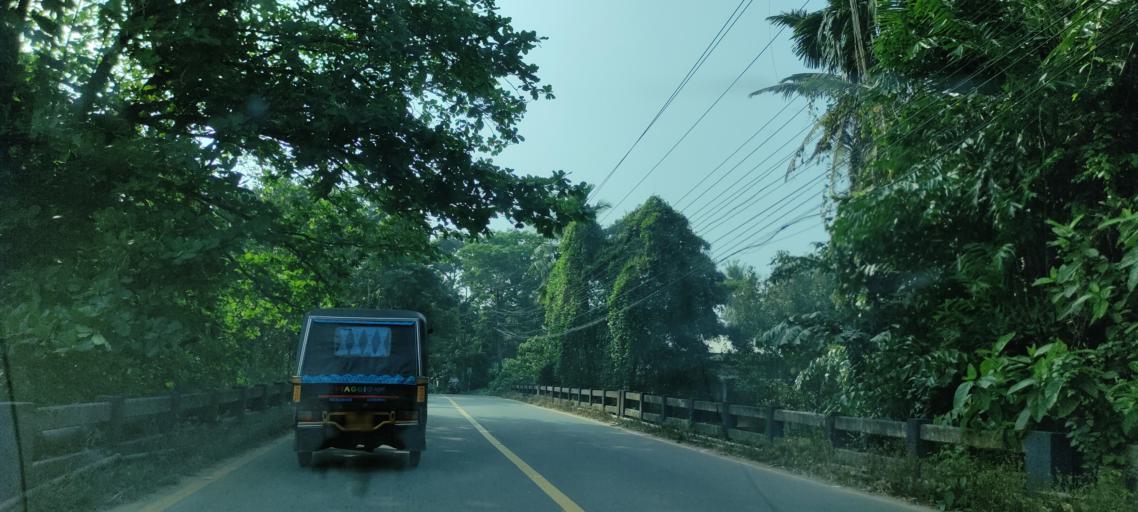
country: IN
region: Kerala
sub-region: Pattanamtitta
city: Tiruvalla
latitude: 9.3694
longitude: 76.5388
